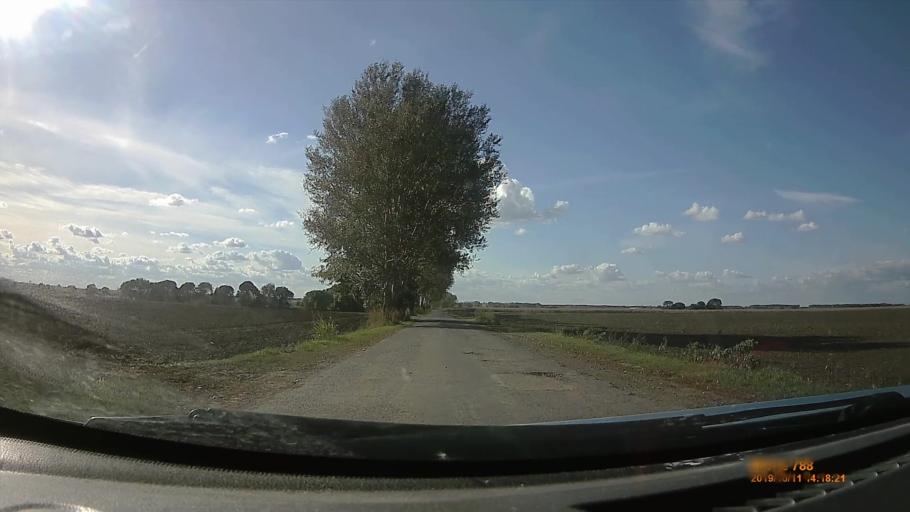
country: HU
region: Hajdu-Bihar
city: Hajduszoboszlo
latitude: 47.5296
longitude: 21.3954
